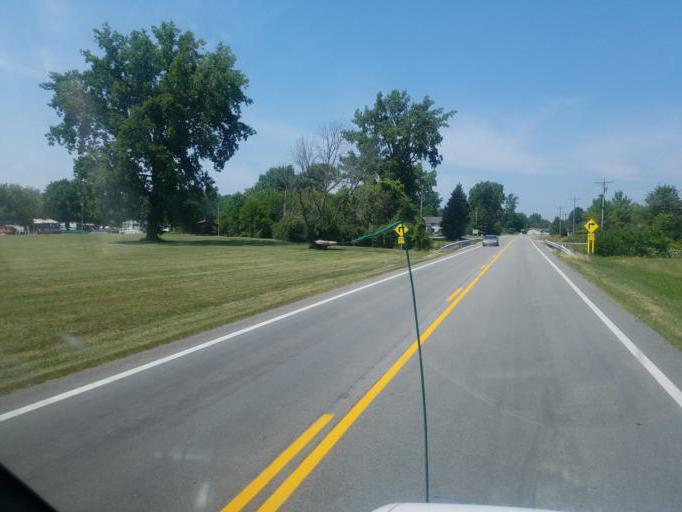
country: US
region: Ohio
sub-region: Auglaize County
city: Saint Marys
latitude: 40.5069
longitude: -84.4345
